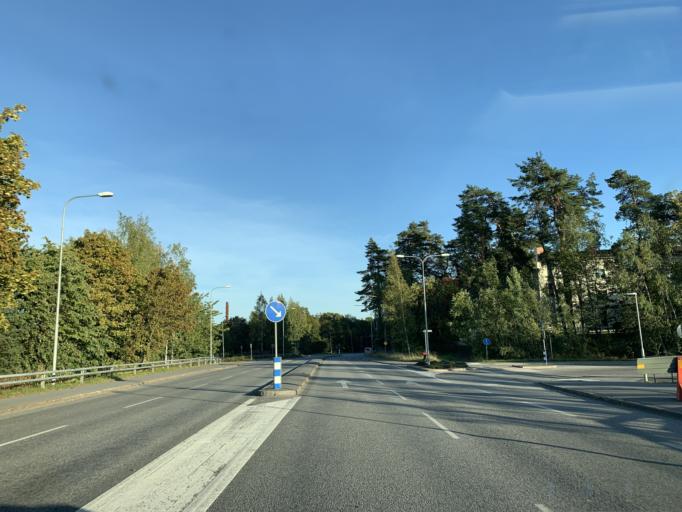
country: SE
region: Stockholm
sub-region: Taby Kommun
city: Taby
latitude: 59.4370
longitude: 18.0606
